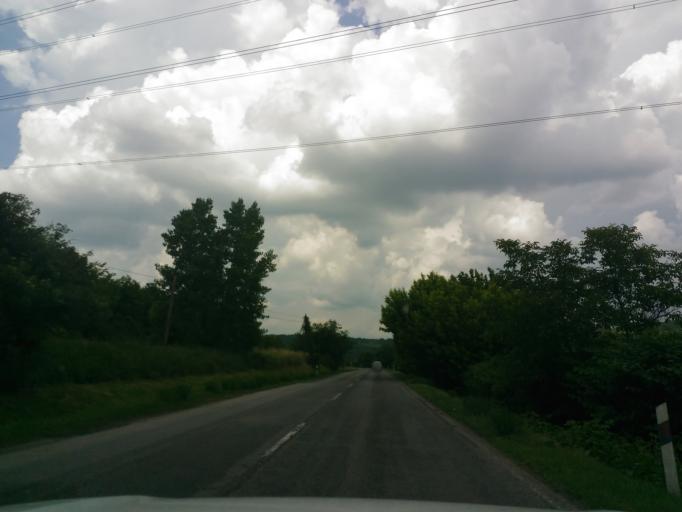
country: HU
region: Baranya
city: Mecseknadasd
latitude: 46.2366
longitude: 18.4789
